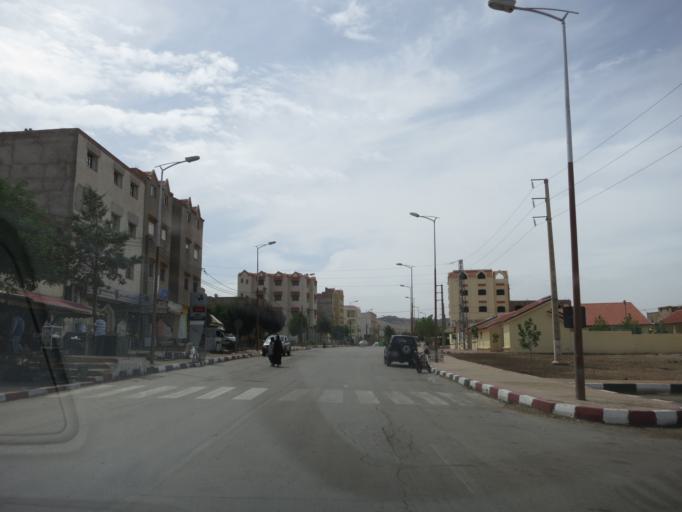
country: MA
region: Meknes-Tafilalet
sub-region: Ifrane
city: Azrou
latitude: 33.2350
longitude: -5.0585
